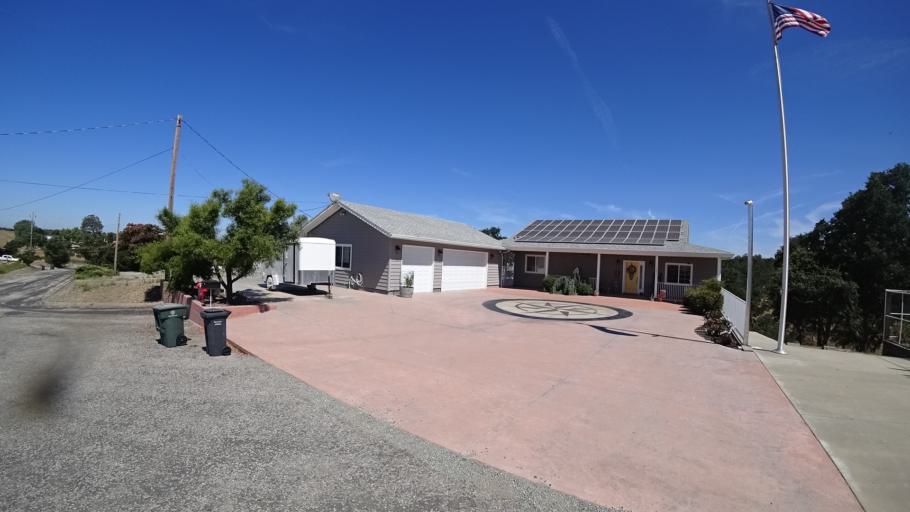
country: US
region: California
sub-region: Calaveras County
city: Valley Springs
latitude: 38.1560
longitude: -120.8307
